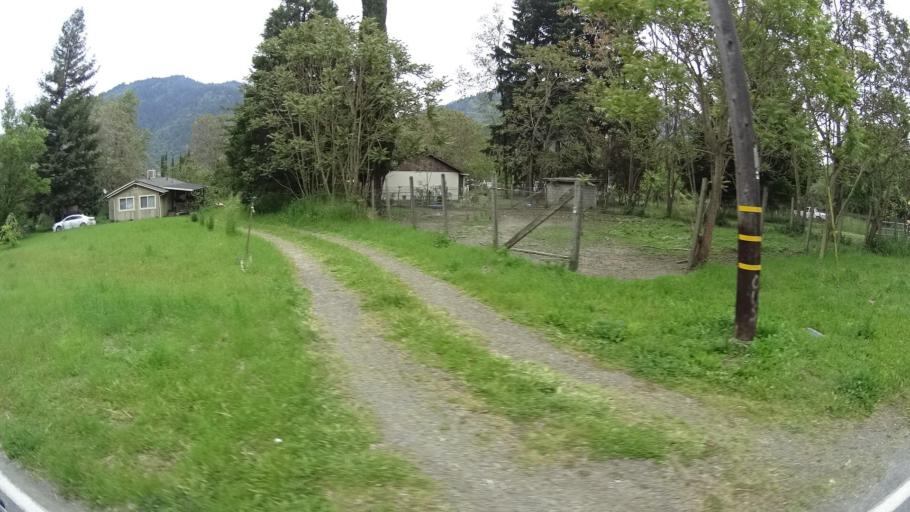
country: US
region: California
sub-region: Humboldt County
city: Willow Creek
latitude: 41.0728
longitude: -123.6943
